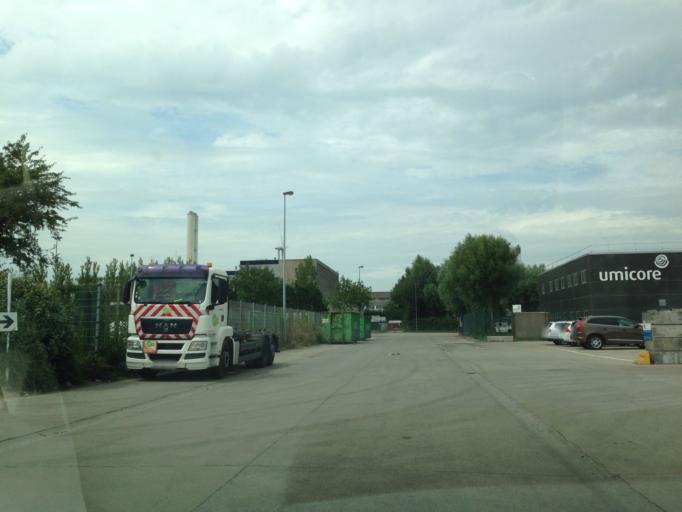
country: BE
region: Flanders
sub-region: Provincie West-Vlaanderen
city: Brugge
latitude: 51.2496
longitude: 3.2091
